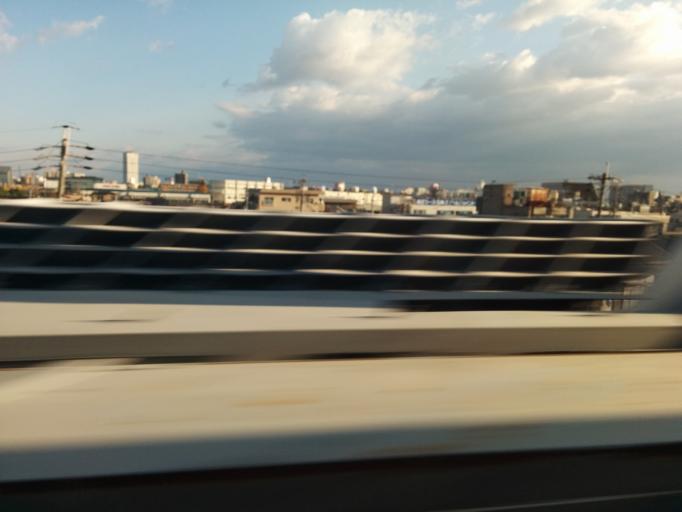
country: JP
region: Aichi
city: Nagoya-shi
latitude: 35.1152
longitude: 136.8972
